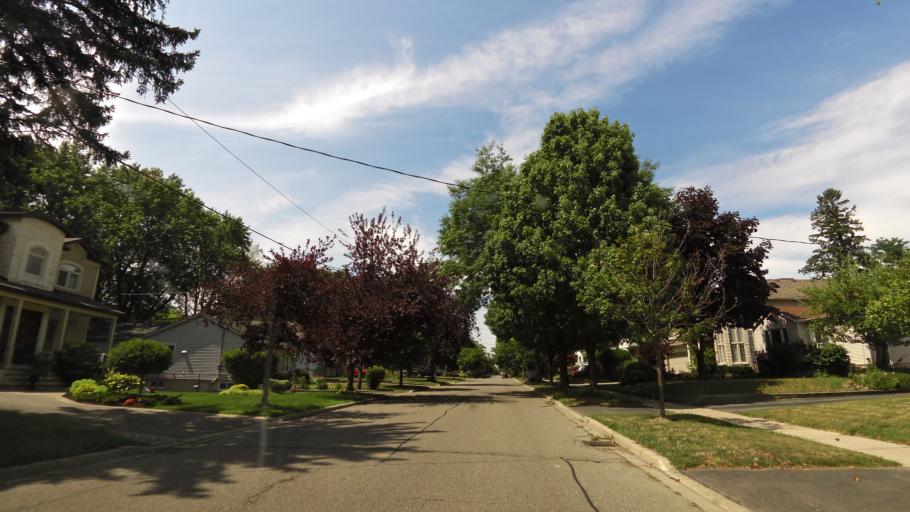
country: CA
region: Ontario
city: Mississauga
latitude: 43.5723
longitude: -79.5820
